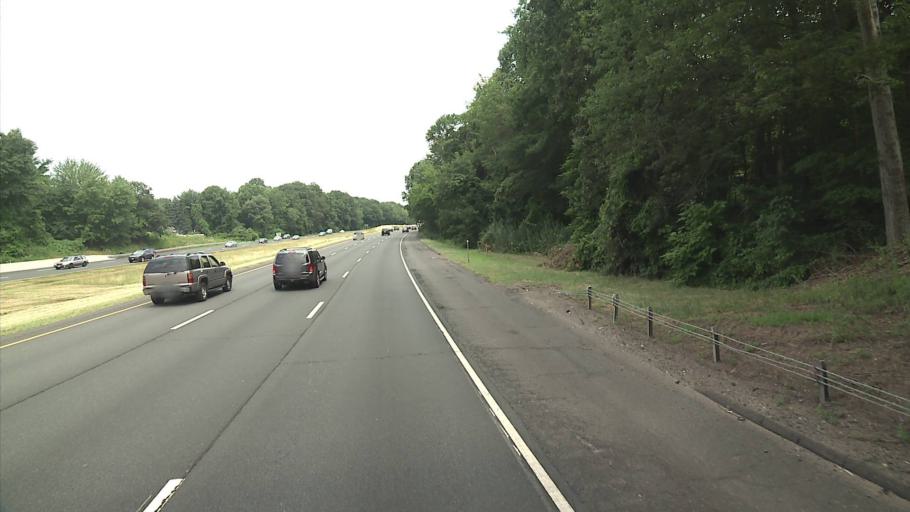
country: US
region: Connecticut
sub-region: New Haven County
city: Wolcott
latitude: 41.5919
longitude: -72.9026
